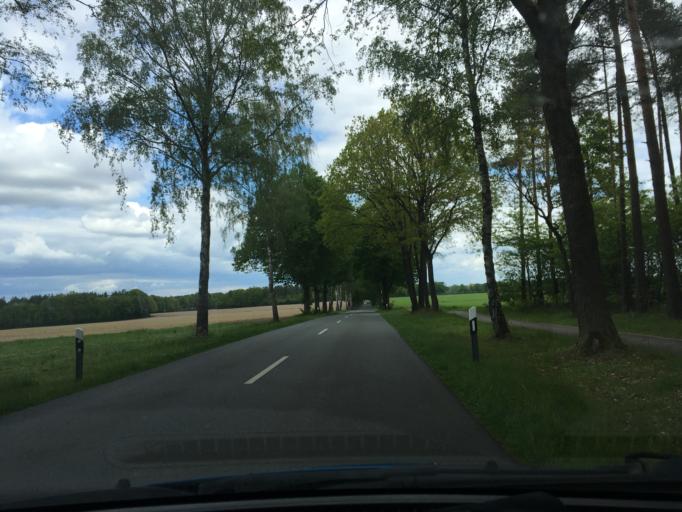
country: DE
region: Lower Saxony
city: Suderburg
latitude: 52.8760
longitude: 10.4370
